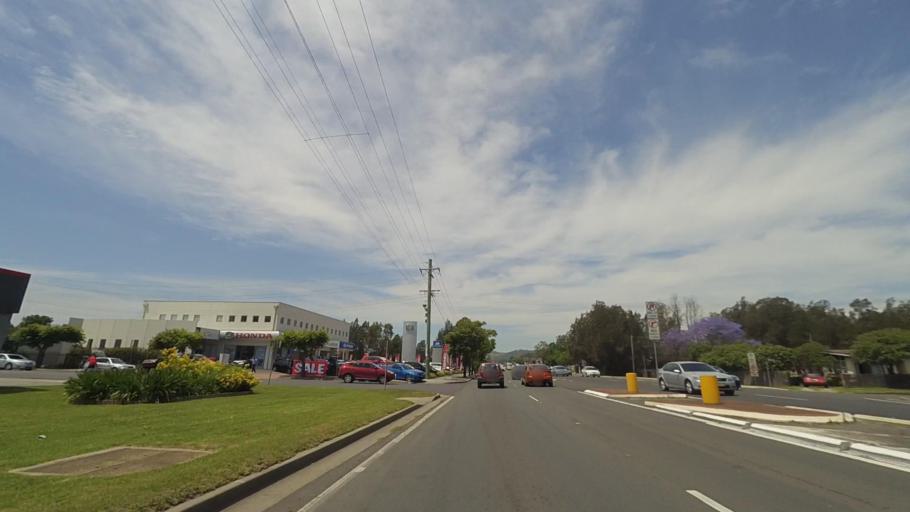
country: AU
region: New South Wales
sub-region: Shellharbour
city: Albion Park Rail
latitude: -34.5549
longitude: 150.7906
